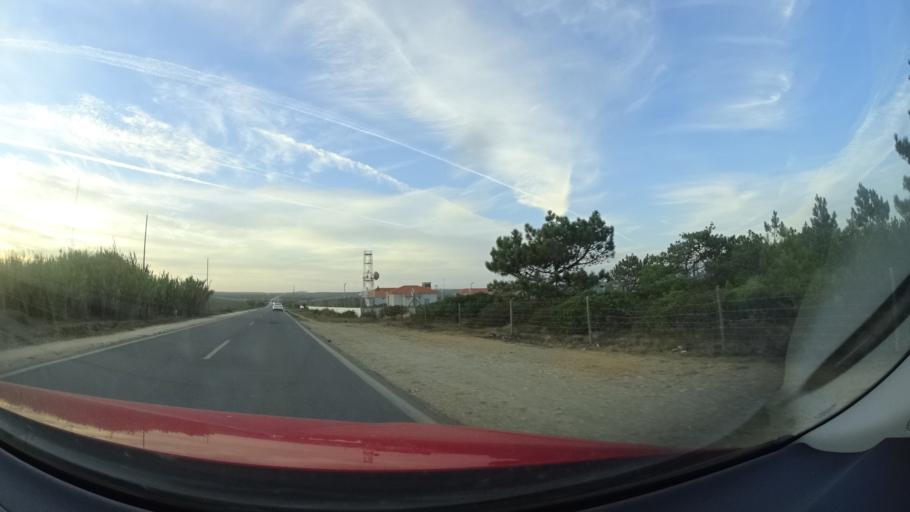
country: PT
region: Faro
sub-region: Vila do Bispo
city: Sagres
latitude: 37.0104
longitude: -8.9498
